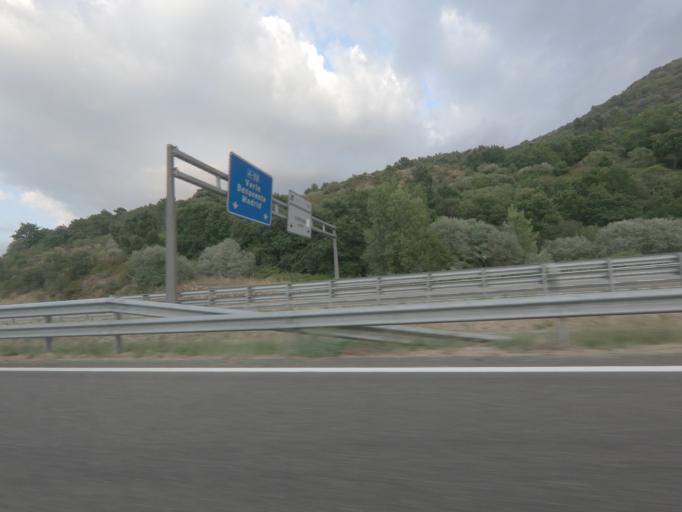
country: ES
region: Galicia
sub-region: Provincia de Ourense
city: Toen
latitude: 42.3425
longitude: -7.9272
